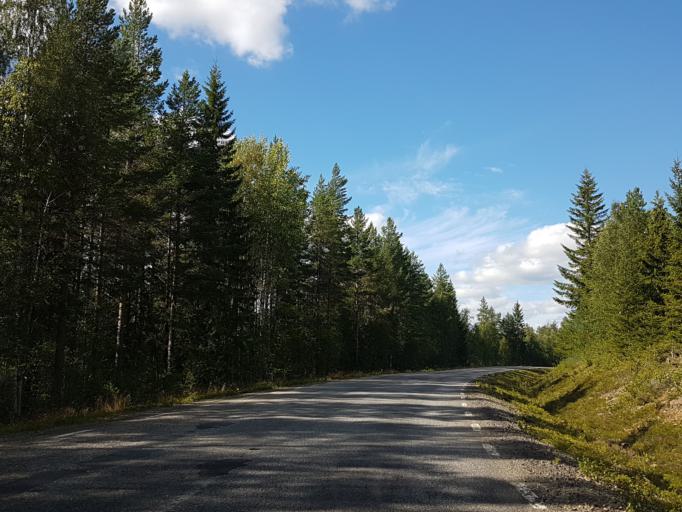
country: SE
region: Vaesterbotten
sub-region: Umea Kommun
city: Saevar
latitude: 64.2229
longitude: 20.4697
